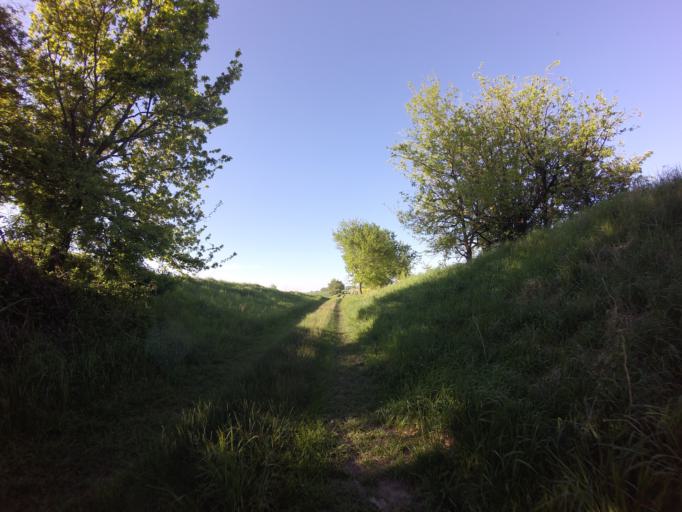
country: PL
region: West Pomeranian Voivodeship
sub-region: Powiat choszczenski
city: Choszczno
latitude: 53.1452
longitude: 15.3637
